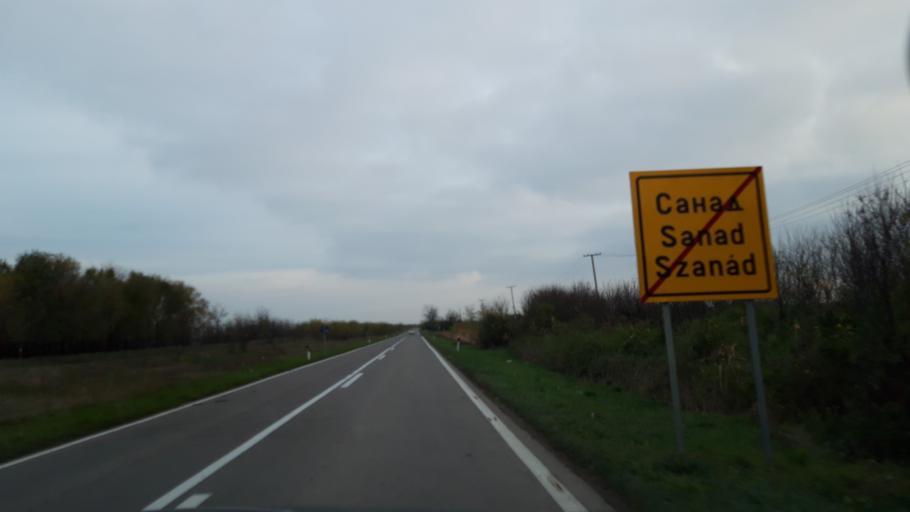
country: RS
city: Sanad
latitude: 45.9746
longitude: 20.1195
